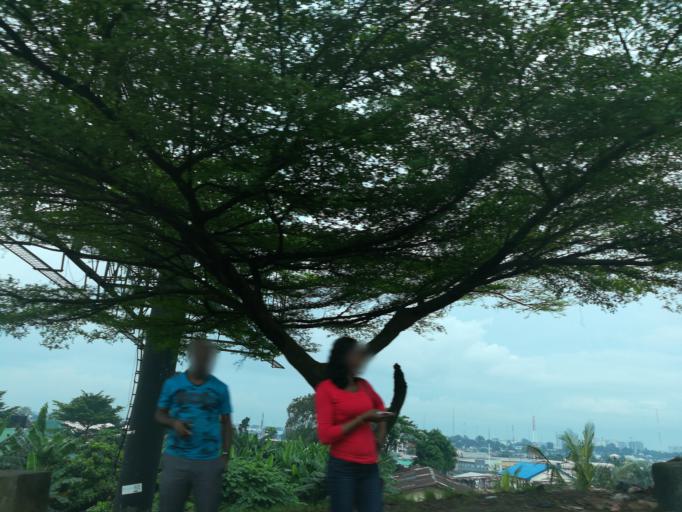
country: NG
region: Rivers
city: Port Harcourt
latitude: 4.8100
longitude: 7.0102
